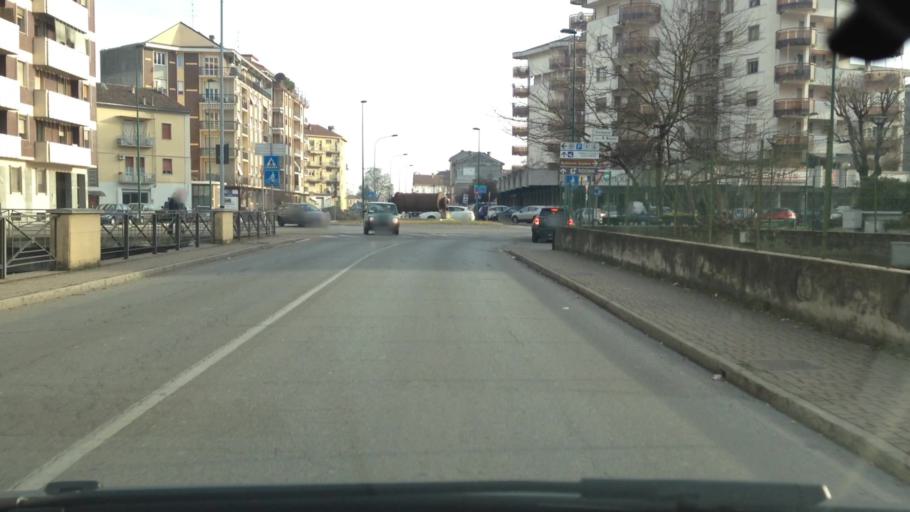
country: IT
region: Piedmont
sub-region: Provincia di Alessandria
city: Casale Monferrato
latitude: 45.1307
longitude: 8.4481
